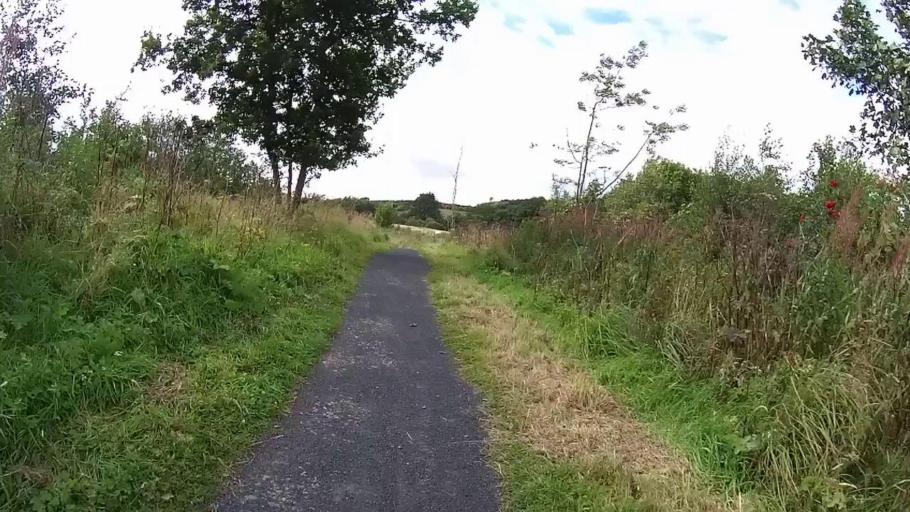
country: GB
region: Scotland
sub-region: Fife
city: Glenrothes
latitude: 56.2195
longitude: -3.1722
